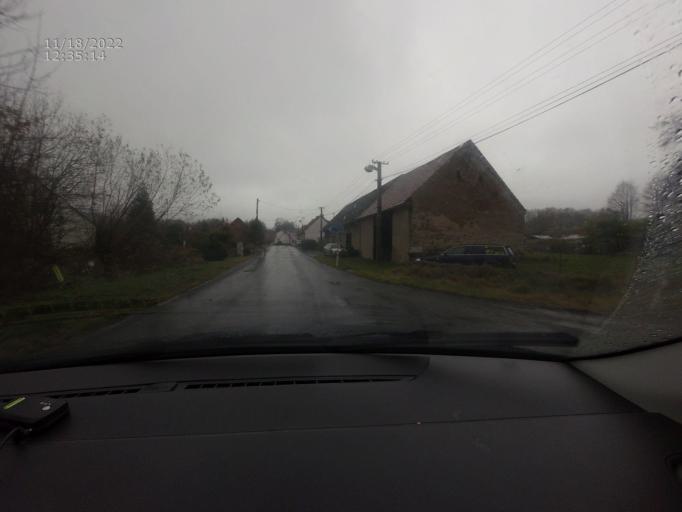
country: CZ
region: Plzensky
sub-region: Okres Klatovy
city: Planice
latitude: 49.4133
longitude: 13.5115
